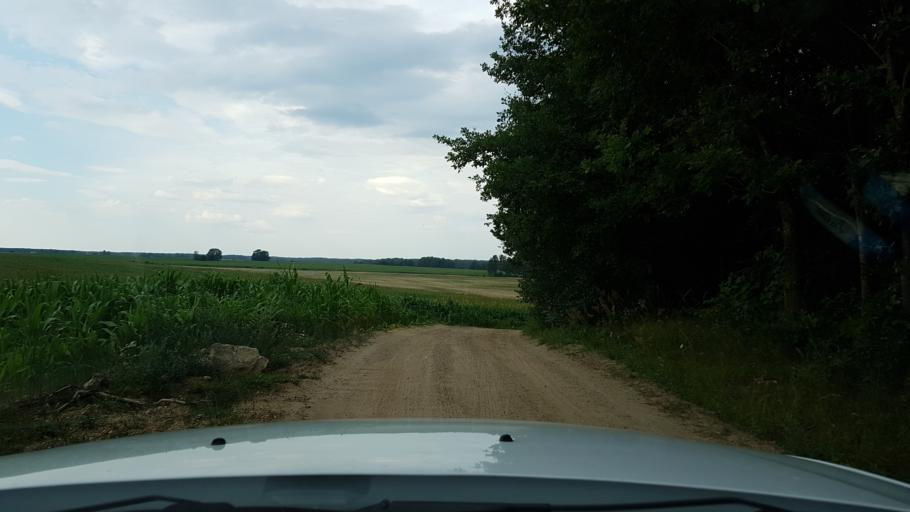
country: PL
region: West Pomeranian Voivodeship
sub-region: Powiat walecki
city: Walcz
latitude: 53.3703
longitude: 16.3409
